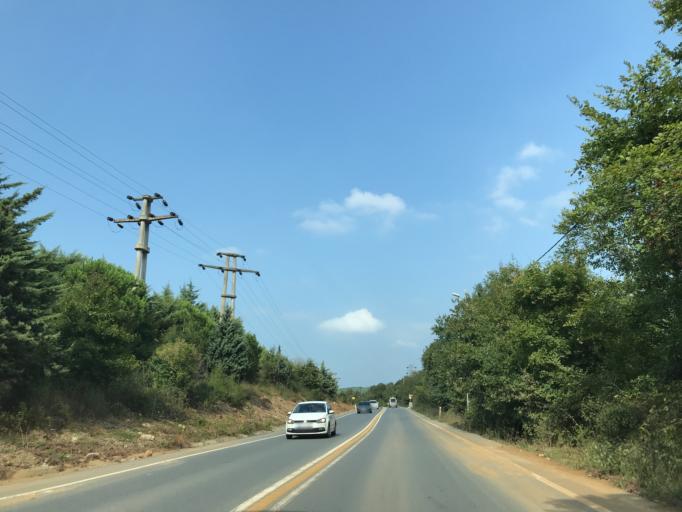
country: TR
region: Istanbul
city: Arikoey
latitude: 41.2273
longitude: 29.0371
